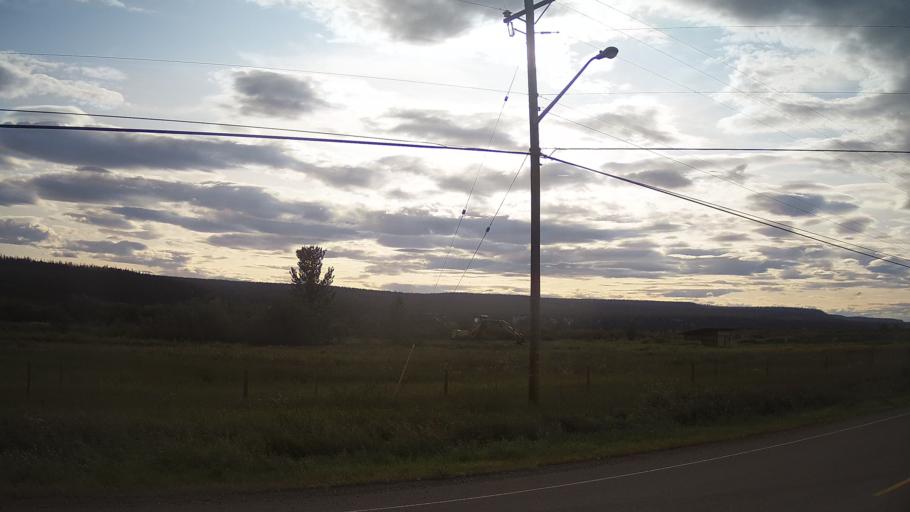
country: CA
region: British Columbia
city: Hanceville
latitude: 52.0120
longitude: -123.1727
